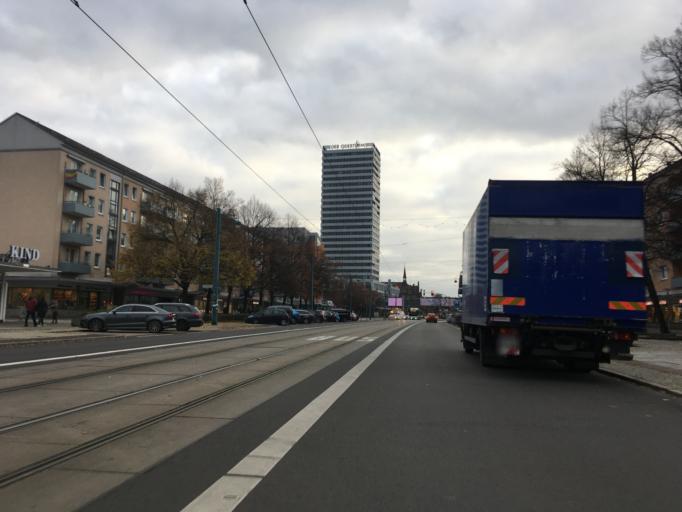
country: DE
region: Brandenburg
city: Frankfurt (Oder)
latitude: 52.3450
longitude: 14.5510
